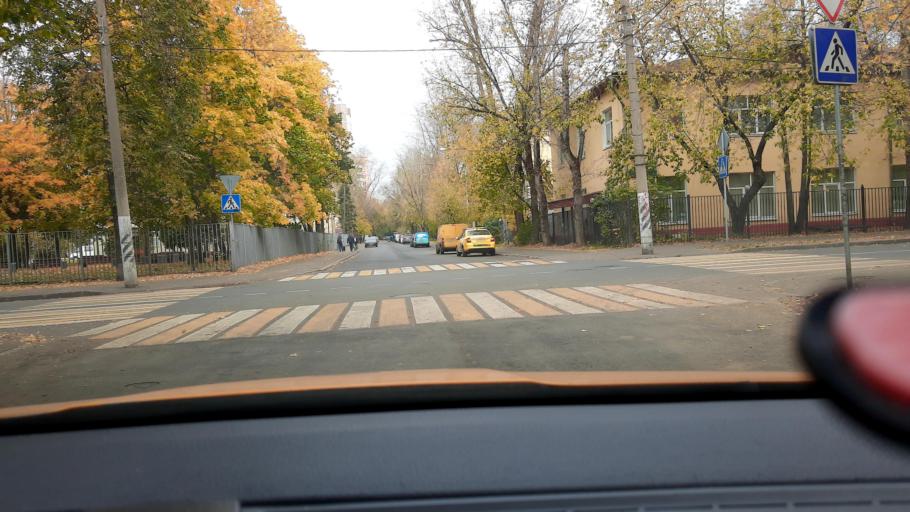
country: RU
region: Moscow
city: Leonovo
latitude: 55.8592
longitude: 37.6443
